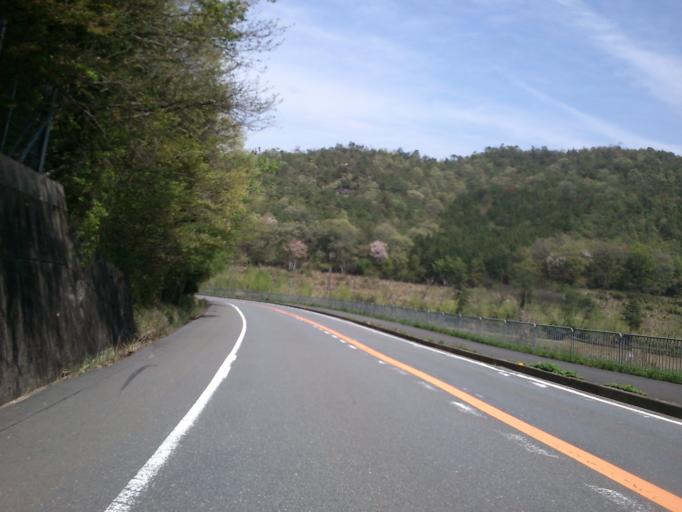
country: JP
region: Kyoto
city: Ayabe
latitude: 35.1652
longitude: 135.3613
